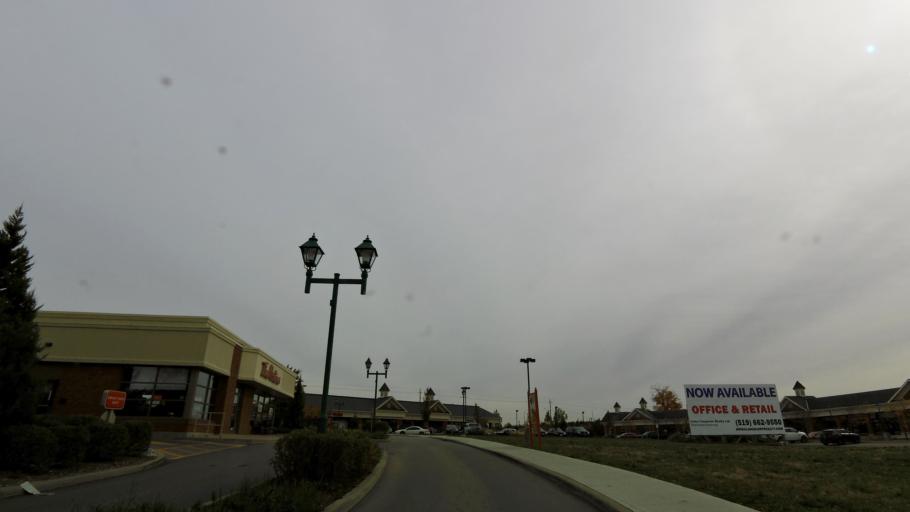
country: CA
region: Ontario
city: Cambridge
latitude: 43.4242
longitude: -80.2864
